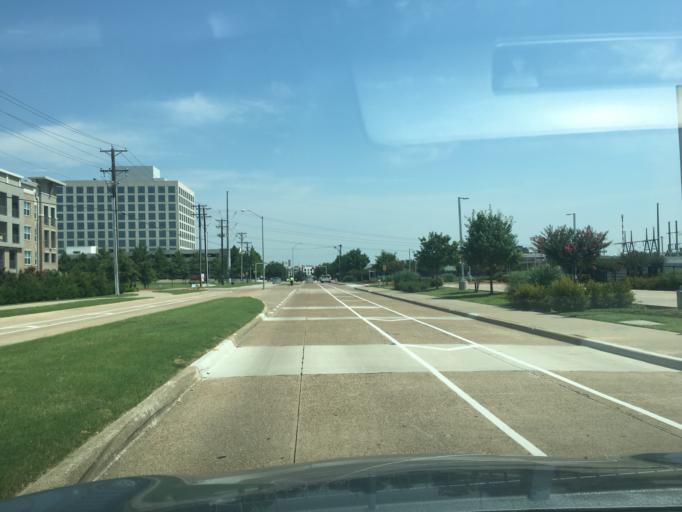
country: US
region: Texas
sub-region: Dallas County
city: Richardson
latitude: 32.9660
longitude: -96.7171
